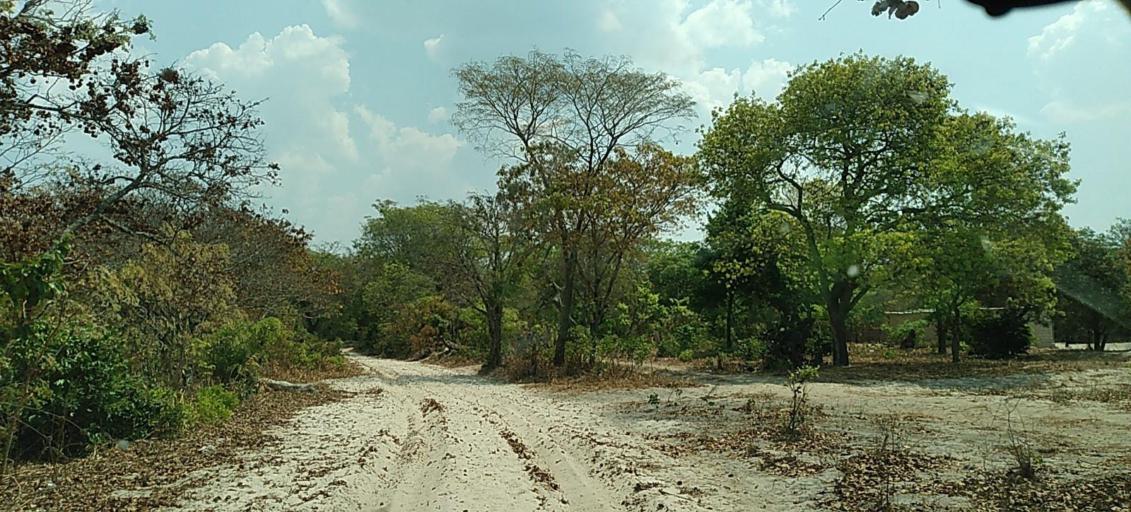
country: ZM
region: North-Western
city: Kabompo
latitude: -13.3592
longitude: 23.8904
